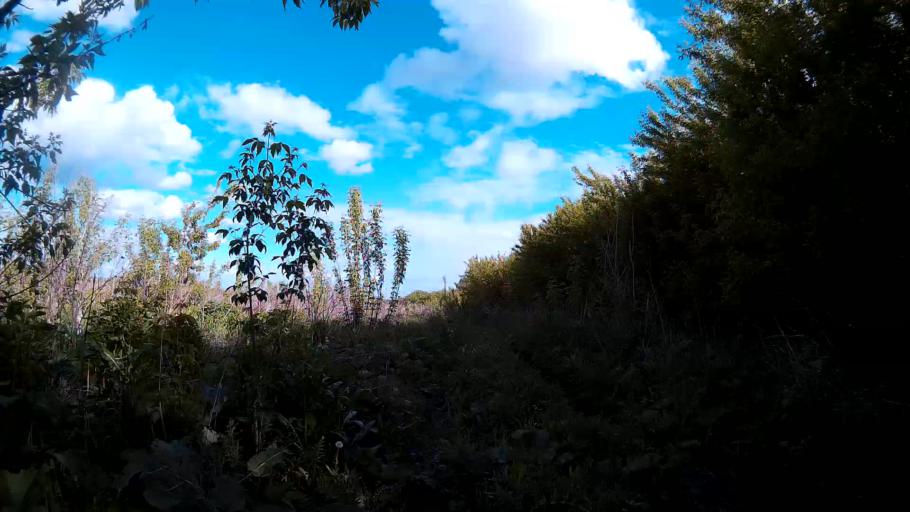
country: RU
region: Ulyanovsk
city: Novoul'yanovsk
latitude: 54.2179
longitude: 48.2571
